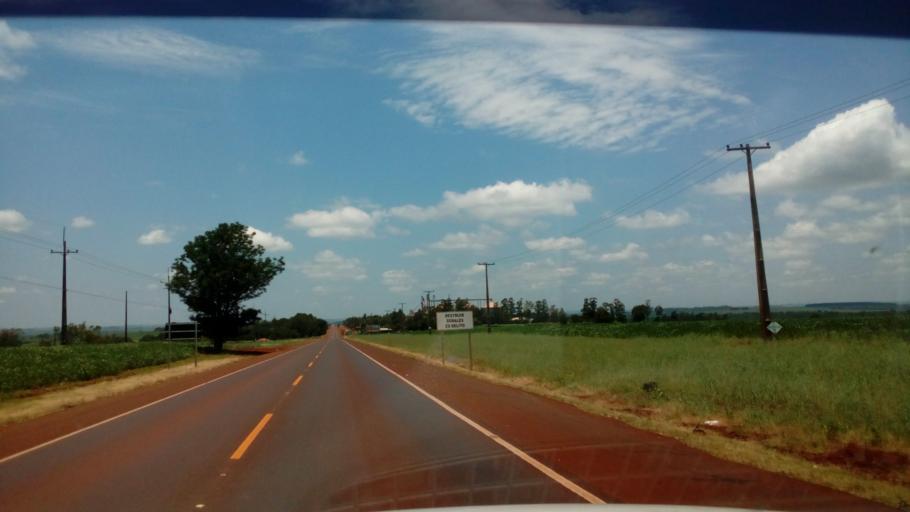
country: PY
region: Alto Parana
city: Naranjal
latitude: -26.0112
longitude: -55.1251
